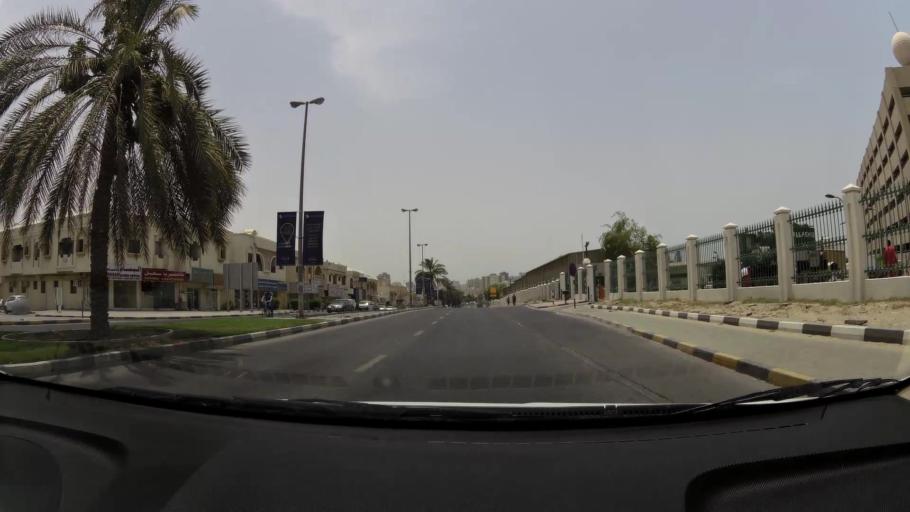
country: AE
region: Ash Shariqah
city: Sharjah
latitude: 25.3546
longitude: 55.4026
